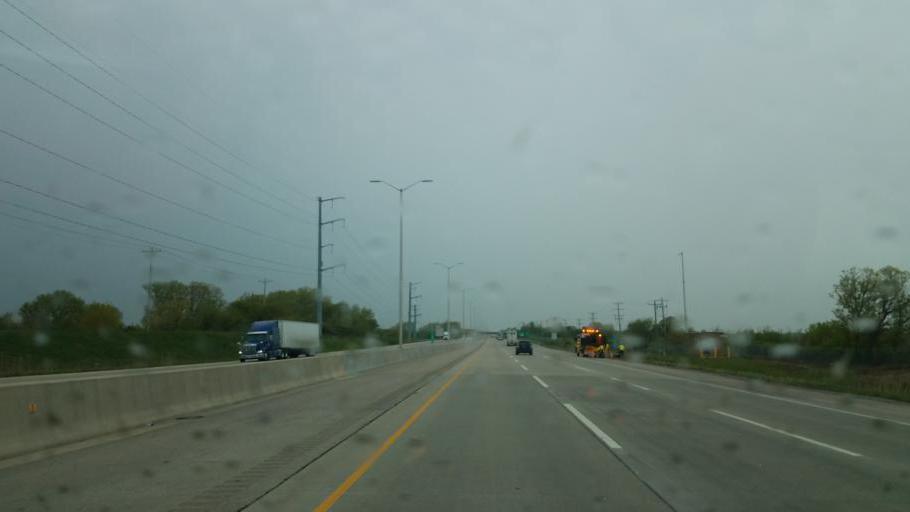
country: US
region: Illinois
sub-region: McHenry County
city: Huntley
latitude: 42.1272
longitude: -88.4451
